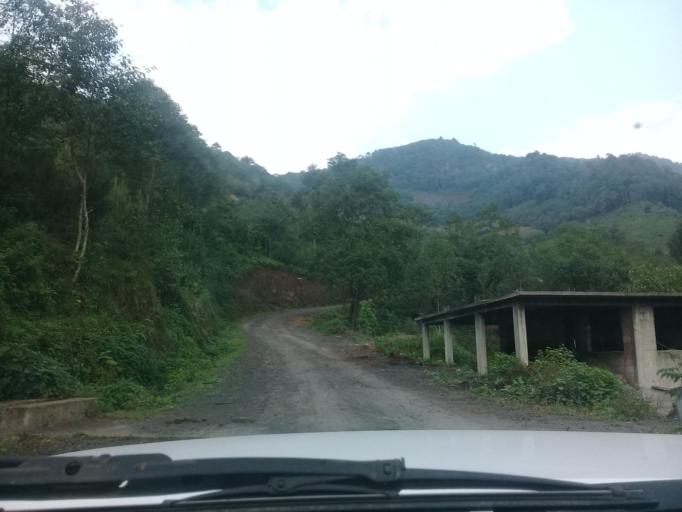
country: MX
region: Veracruz
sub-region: Mariano Escobedo
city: San Isidro el Berro
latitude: 18.9537
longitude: -97.1987
